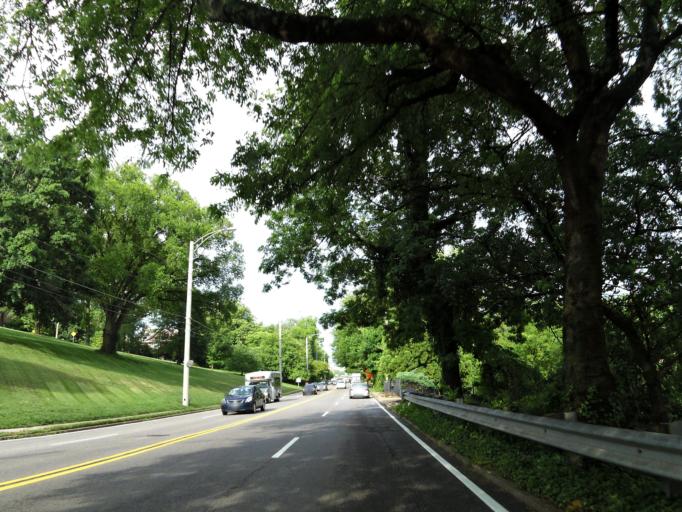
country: US
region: Tennessee
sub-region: Knox County
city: Knoxville
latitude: 35.9510
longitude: -83.9513
